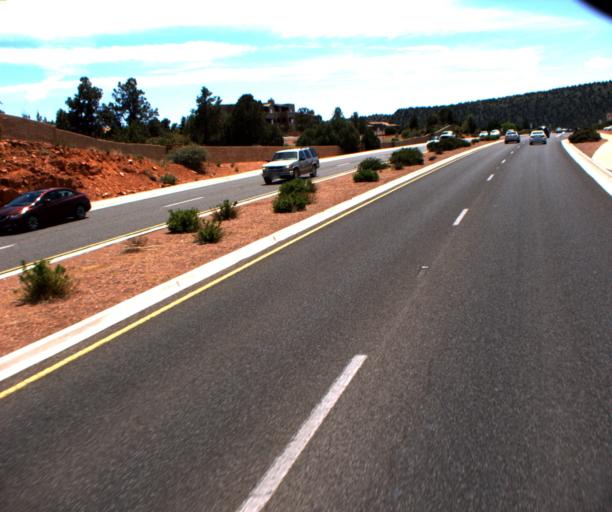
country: US
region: Arizona
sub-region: Yavapai County
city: West Sedona
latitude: 34.8544
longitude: -111.8237
